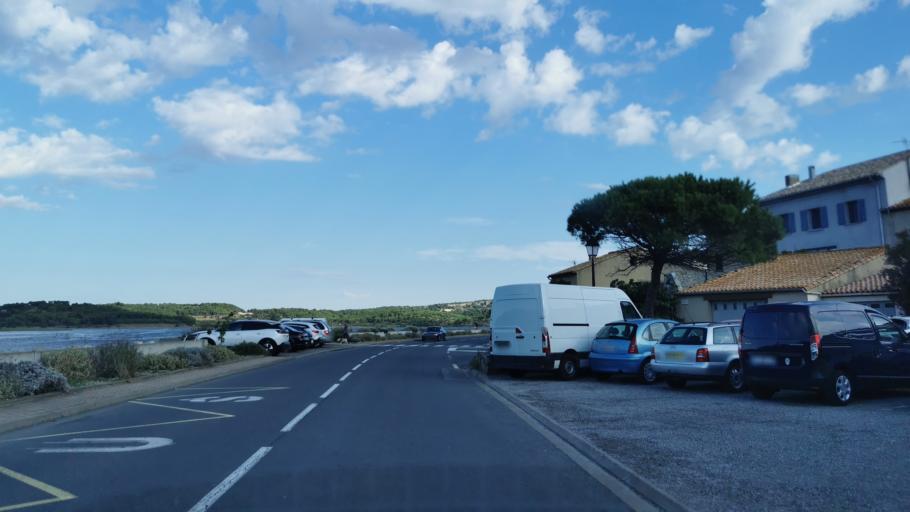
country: FR
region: Languedoc-Roussillon
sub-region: Departement de l'Aude
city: Gruissan
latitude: 43.1063
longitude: 3.0835
